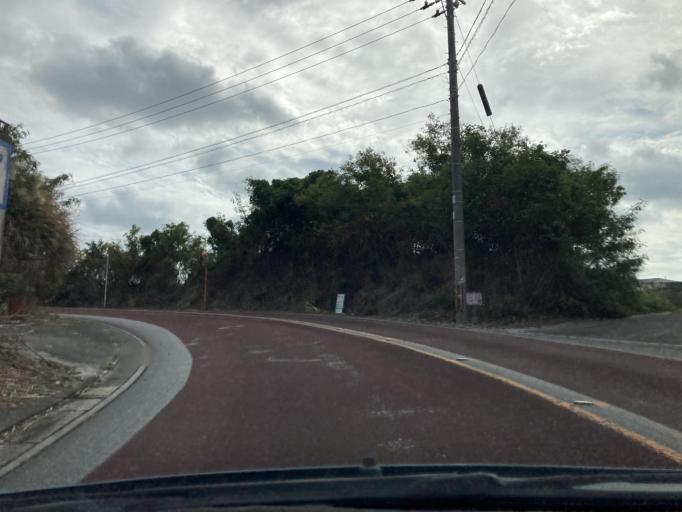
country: JP
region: Okinawa
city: Itoman
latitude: 26.1223
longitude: 127.6780
